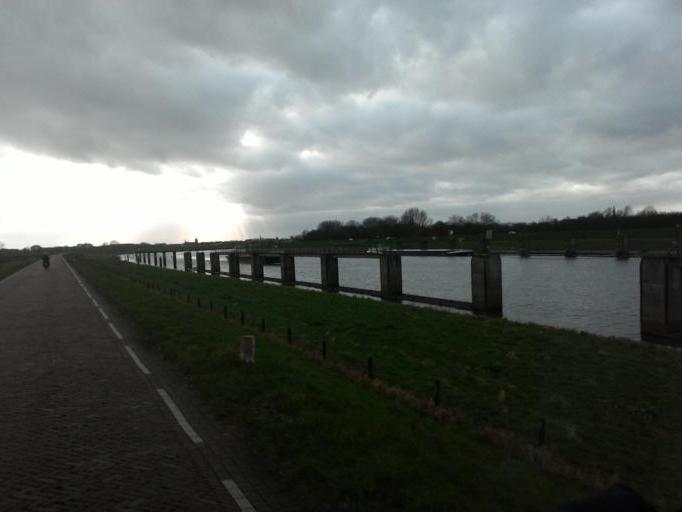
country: NL
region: Utrecht
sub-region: Gemeente Vianen
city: Vianen
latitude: 52.0107
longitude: 5.1093
